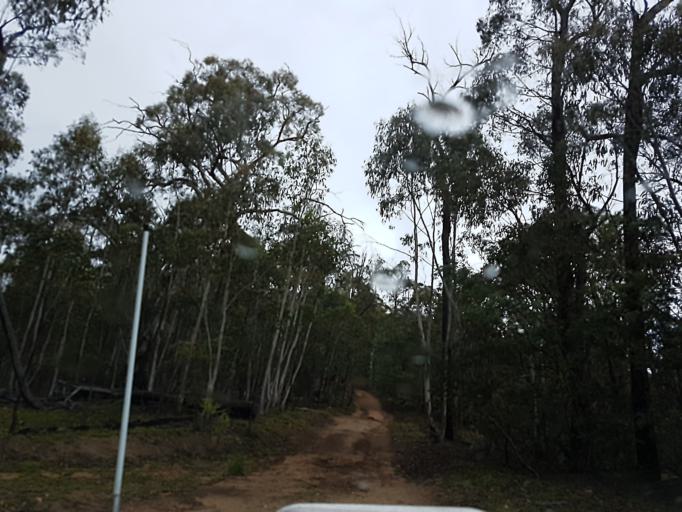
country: AU
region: New South Wales
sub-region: Snowy River
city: Jindabyne
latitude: -36.8679
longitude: 148.3292
